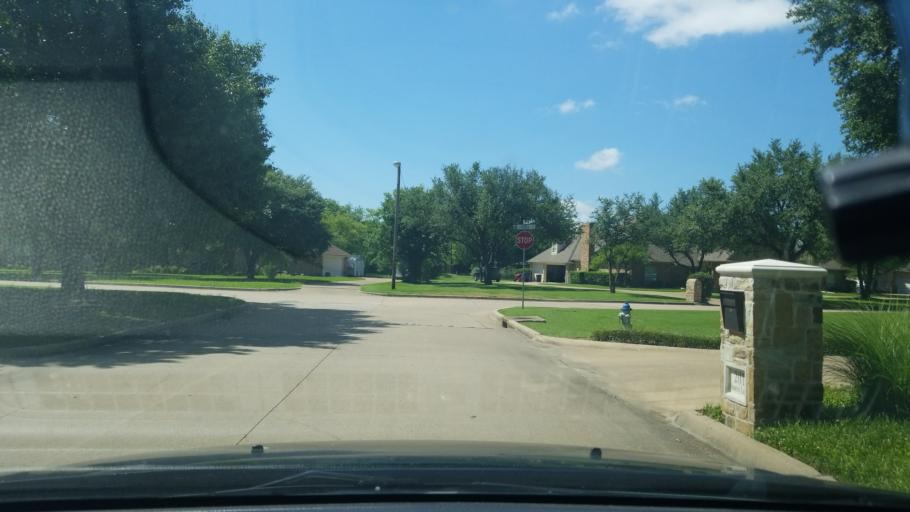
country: US
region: Texas
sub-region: Dallas County
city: Sunnyvale
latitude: 32.7986
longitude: -96.5924
